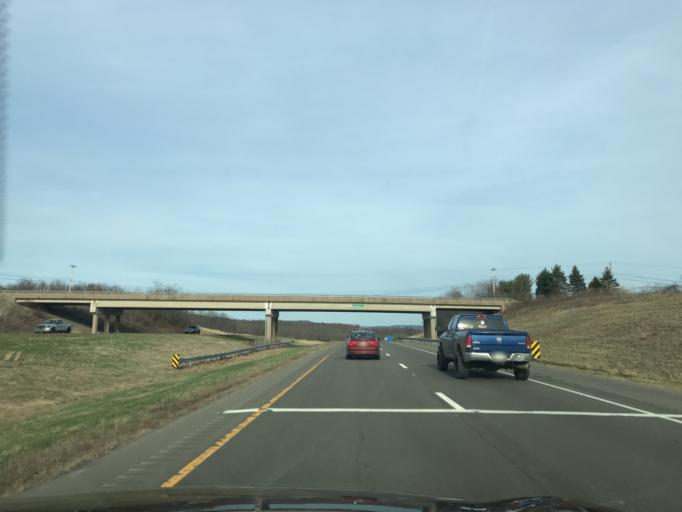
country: US
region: Pennsylvania
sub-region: Lycoming County
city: Montoursville
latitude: 41.2527
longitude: -76.8628
